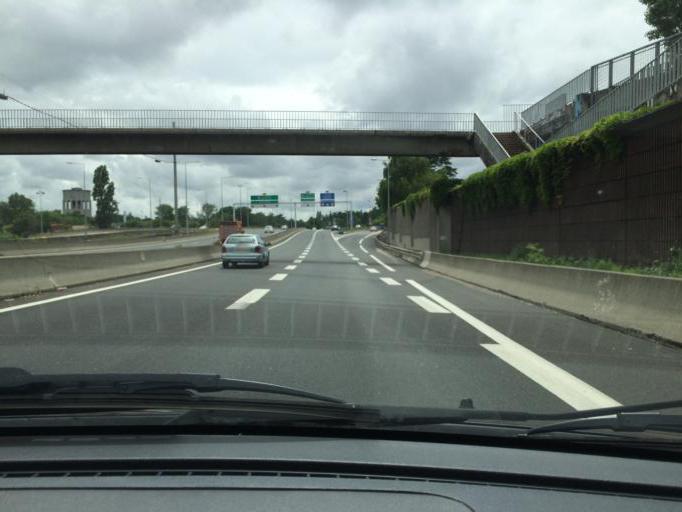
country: FR
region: Rhone-Alpes
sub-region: Departement du Rhone
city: Bron
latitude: 45.7310
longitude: 4.8992
